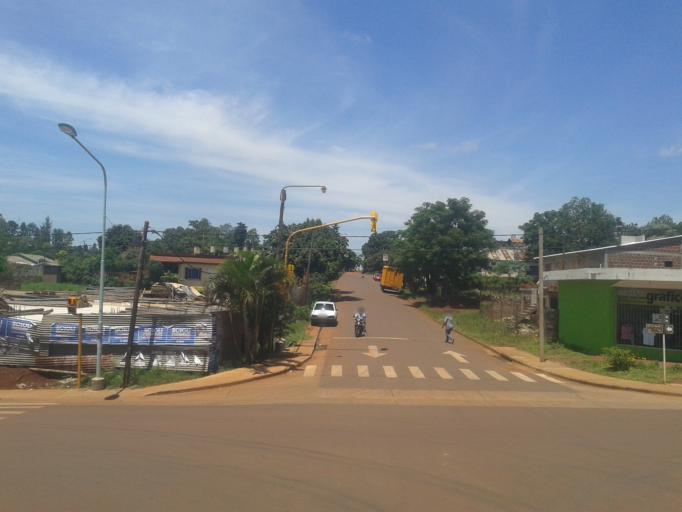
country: AR
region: Misiones
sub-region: Departamento de Leandro N. Alem
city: Leandro N. Alem
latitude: -27.6082
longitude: -55.3327
